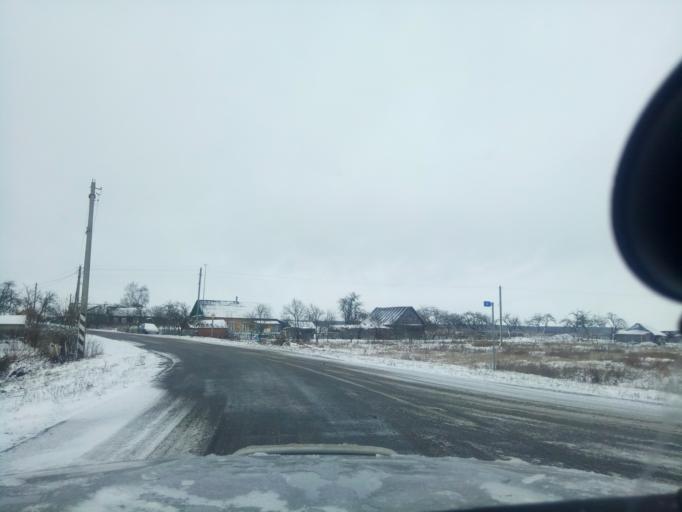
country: BY
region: Minsk
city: Klyetsk
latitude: 53.0087
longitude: 26.7010
